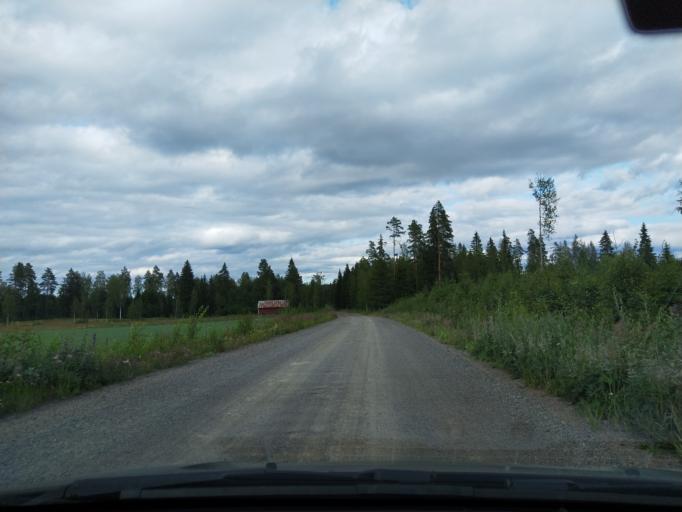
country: FI
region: Kymenlaakso
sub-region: Kouvola
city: Kouvola
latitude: 61.0506
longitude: 26.8592
